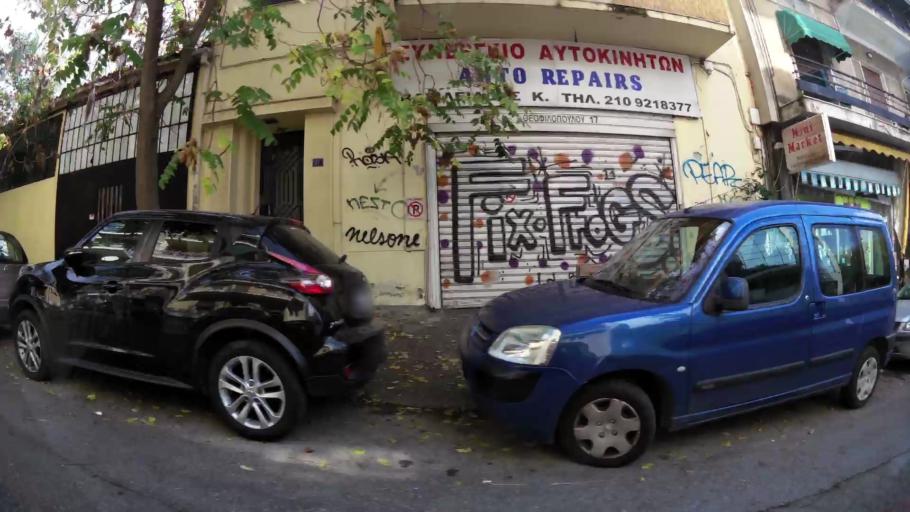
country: GR
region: Attica
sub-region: Nomarchia Athinas
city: Dhafni
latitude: 37.9654
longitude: 23.7312
